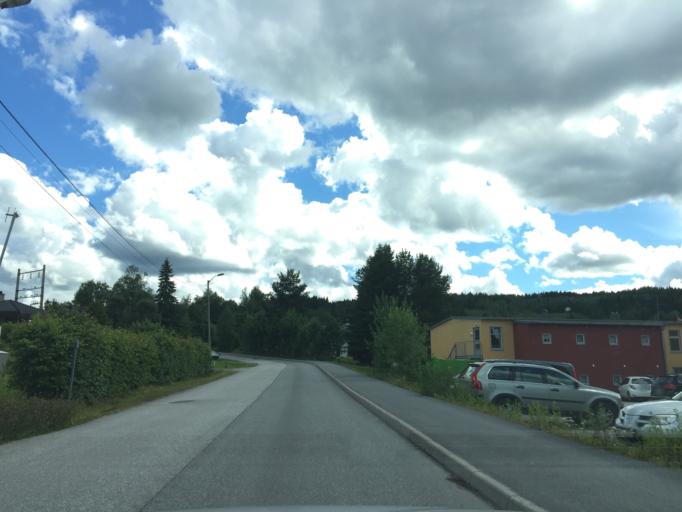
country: NO
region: Hedmark
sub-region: Kongsvinger
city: Kongsvinger
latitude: 60.1836
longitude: 12.0106
